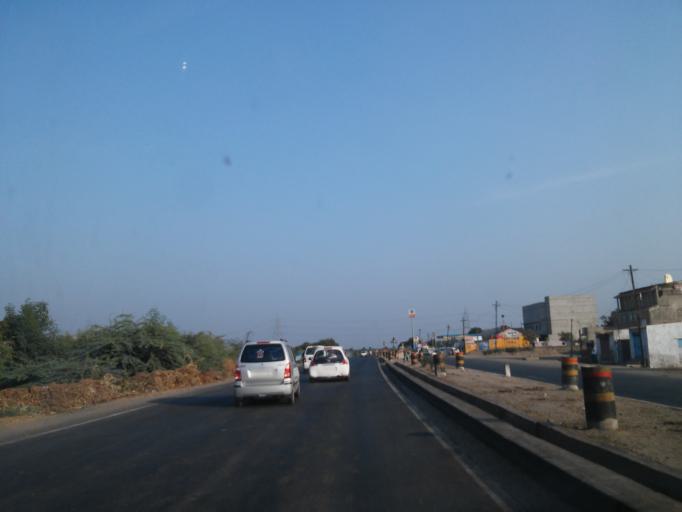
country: IN
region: Gujarat
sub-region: Ahmadabad
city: Mandal
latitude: 23.0965
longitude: 72.1097
